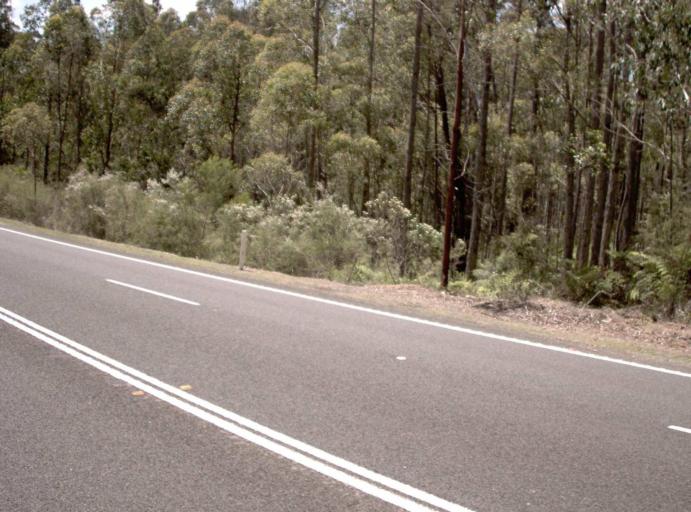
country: AU
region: New South Wales
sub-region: Bombala
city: Bombala
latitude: -37.6150
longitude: 148.8892
